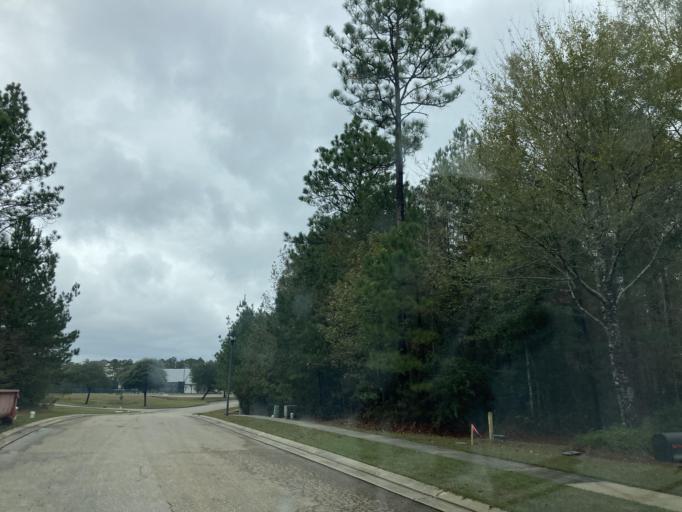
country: US
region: Mississippi
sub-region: Lamar County
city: West Hattiesburg
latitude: 31.2849
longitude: -89.4806
